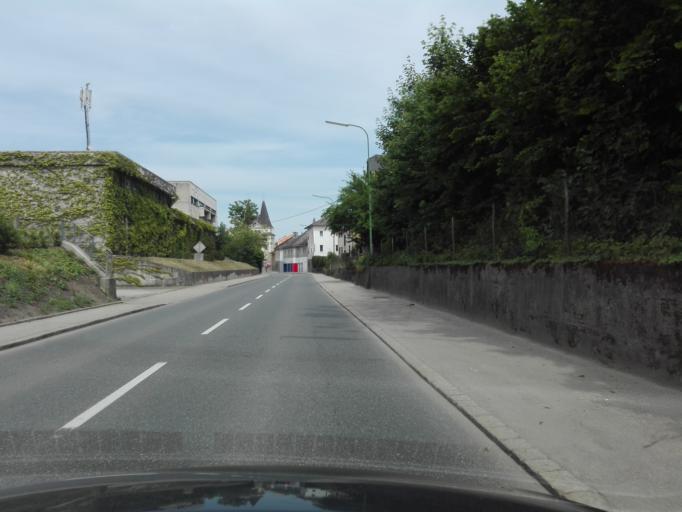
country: AT
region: Upper Austria
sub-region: Politischer Bezirk Vocklabruck
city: Schwanenstadt
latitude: 48.0527
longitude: 13.7701
